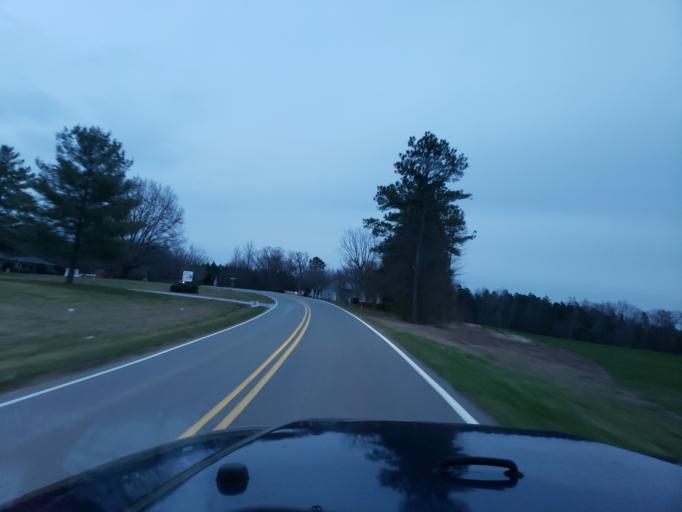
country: US
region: North Carolina
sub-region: Cleveland County
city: White Plains
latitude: 35.1852
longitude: -81.4298
